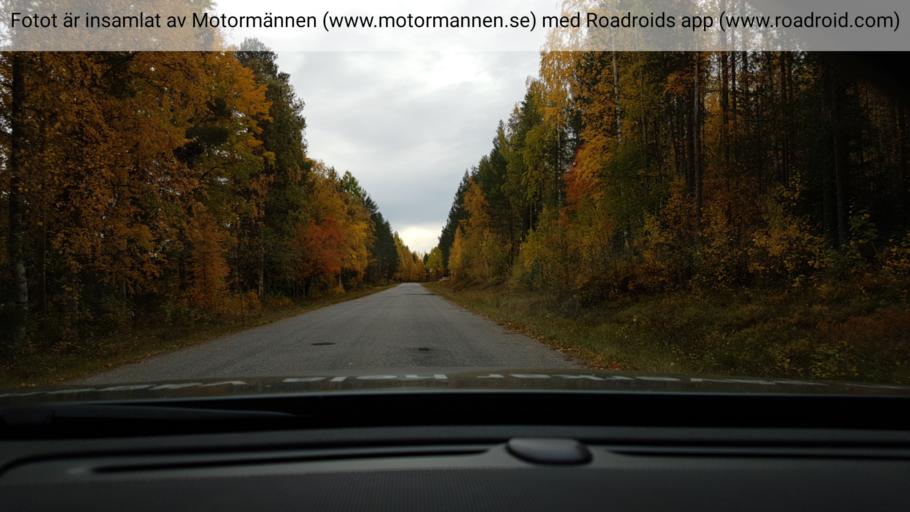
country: SE
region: Norrbotten
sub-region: Overkalix Kommun
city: OEverkalix
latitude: 66.2364
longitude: 23.0082
